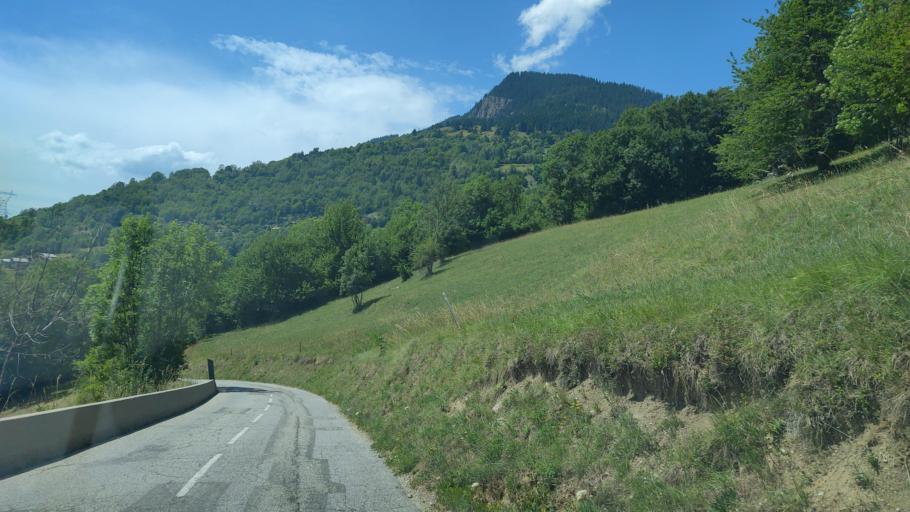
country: FR
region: Rhone-Alpes
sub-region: Departement de la Savoie
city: Bozel
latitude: 45.4505
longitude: 6.6534
